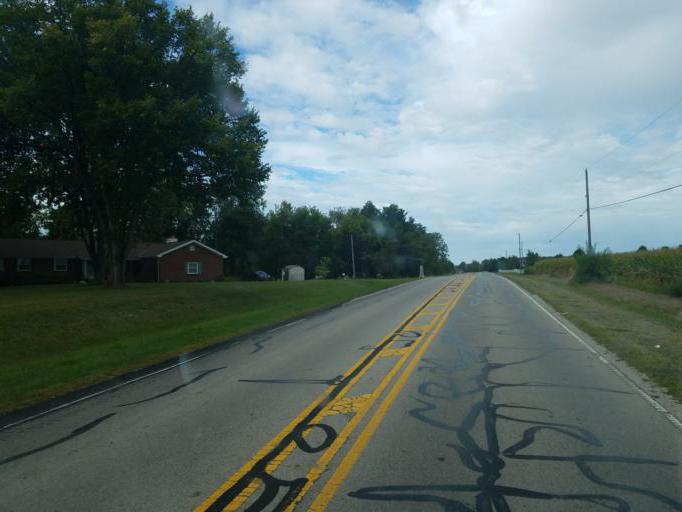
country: US
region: Ohio
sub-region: Delaware County
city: Sunbury
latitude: 40.2270
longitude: -82.7922
